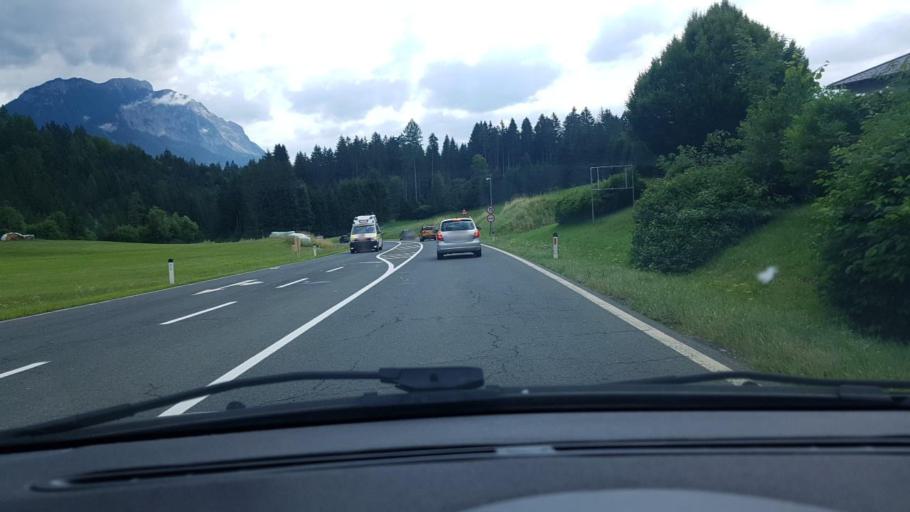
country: AT
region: Carinthia
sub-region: Politischer Bezirk Villach Land
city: Feistritz an der Gail
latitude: 46.6052
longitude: 13.5567
